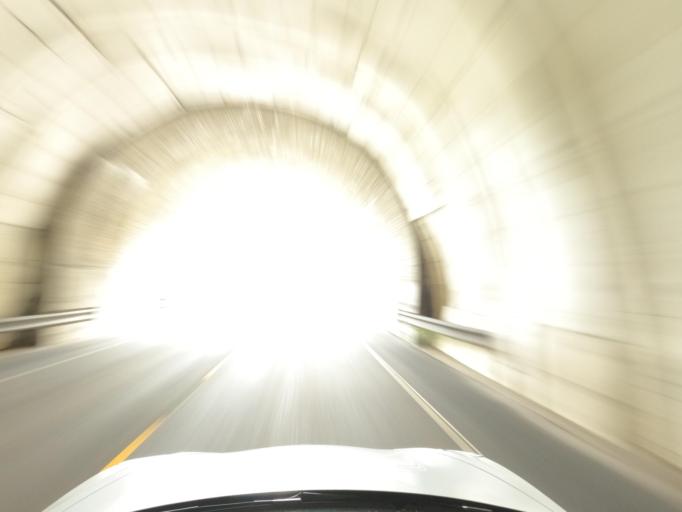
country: NO
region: Telemark
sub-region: Hjartdal
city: Sauland
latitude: 59.7355
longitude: 9.0191
